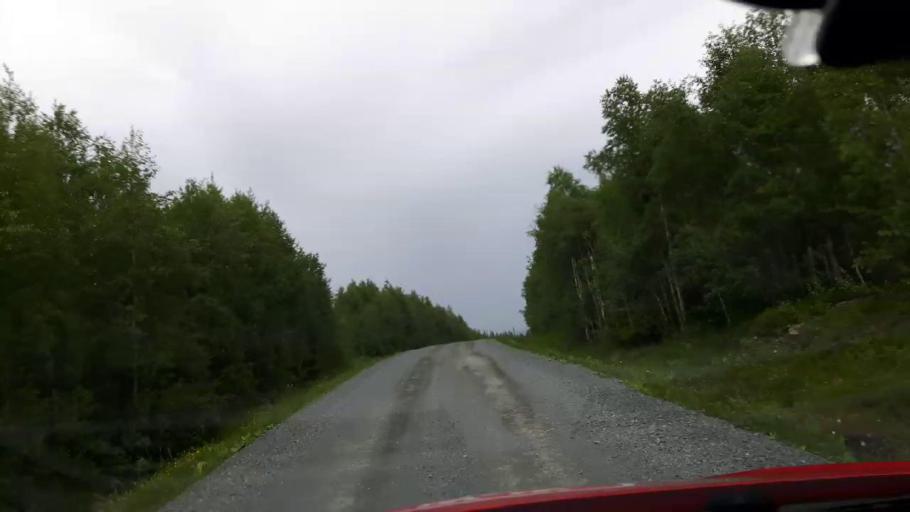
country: NO
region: Nord-Trondelag
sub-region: Lierne
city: Sandvika
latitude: 64.1531
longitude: 13.9835
